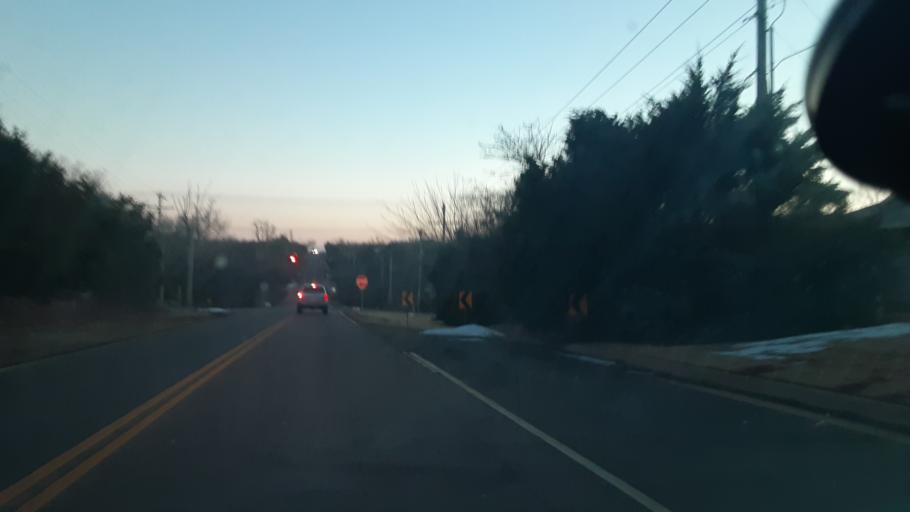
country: US
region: Oklahoma
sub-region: Oklahoma County
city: Edmond
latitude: 35.7114
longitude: -97.4252
